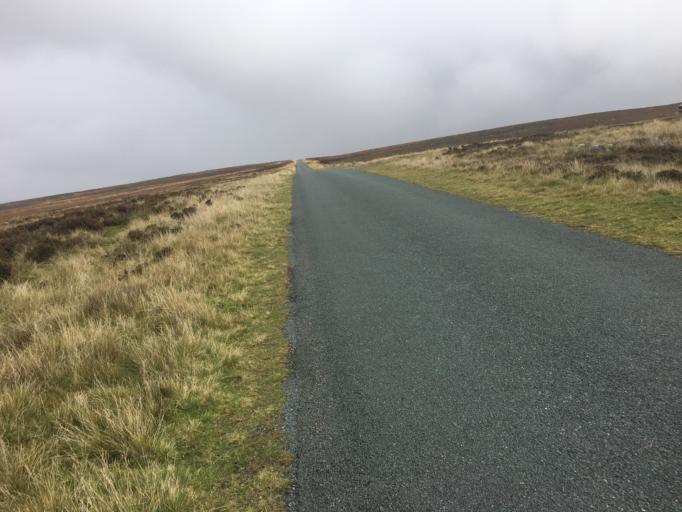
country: GB
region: England
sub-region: North Yorkshire
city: Danby
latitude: 54.4700
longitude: -0.8768
